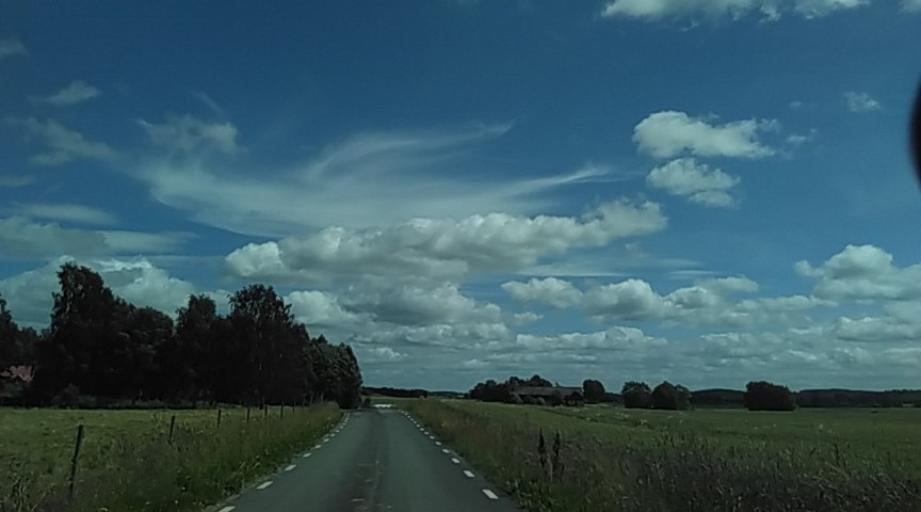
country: SE
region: Vaestra Goetaland
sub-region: Vargarda Kommun
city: Vargarda
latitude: 58.1404
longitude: 12.8378
